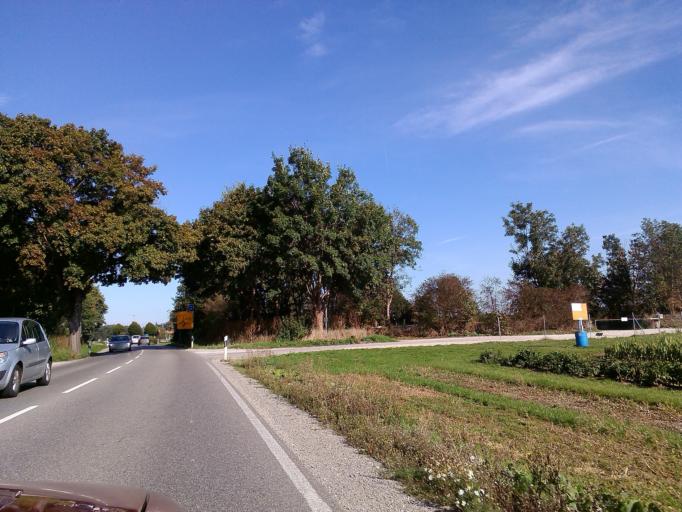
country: DE
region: Bavaria
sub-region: Upper Bavaria
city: Puchheim
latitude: 48.1553
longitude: 11.3366
